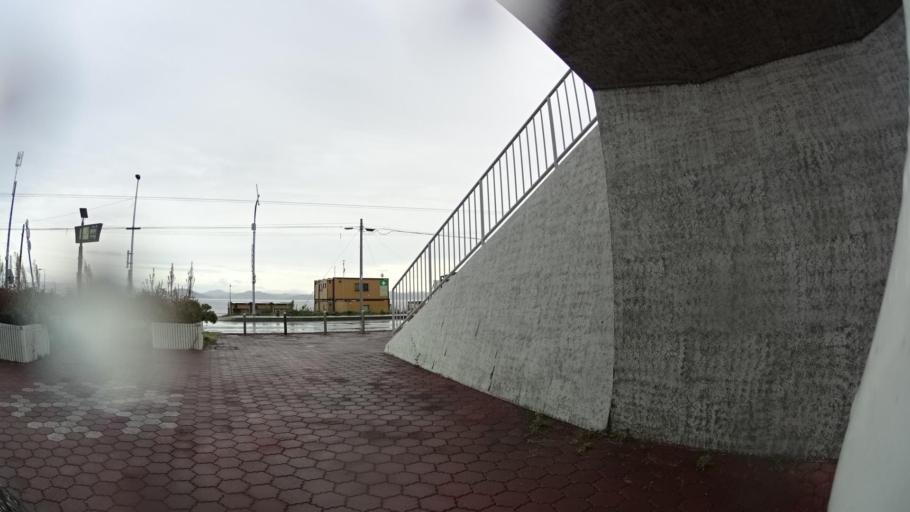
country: JP
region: Hokkaido
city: Kitami
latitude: 44.1862
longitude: 143.7639
